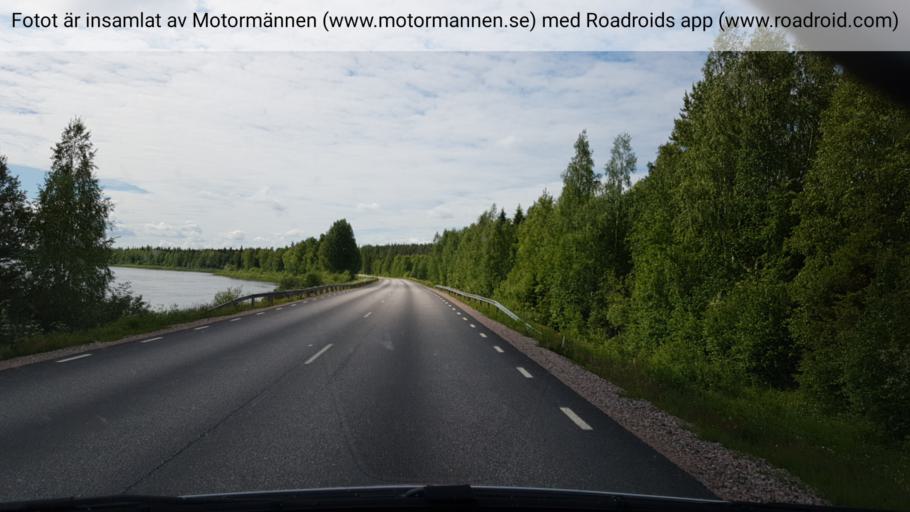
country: SE
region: Norrbotten
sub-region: Overtornea Kommun
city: OEvertornea
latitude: 66.5103
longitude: 23.7296
